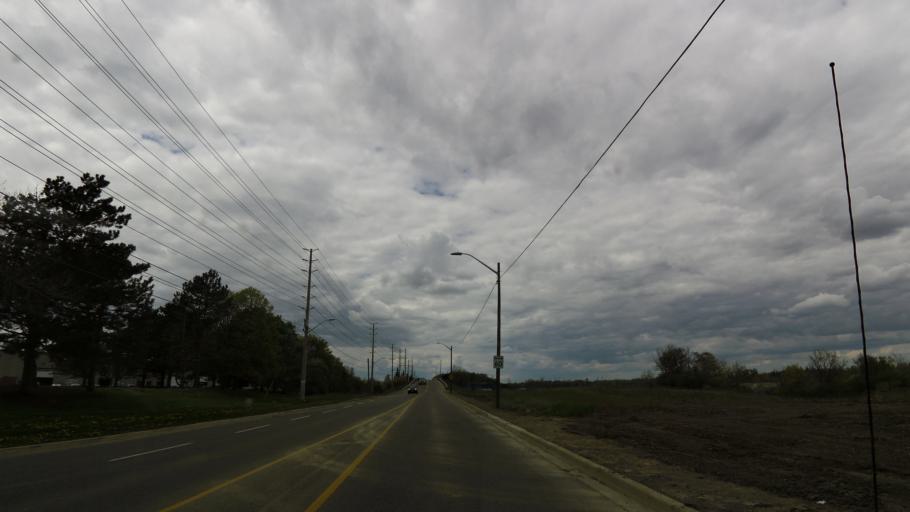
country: CA
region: Ontario
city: Mississauga
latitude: 43.6099
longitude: -79.7287
